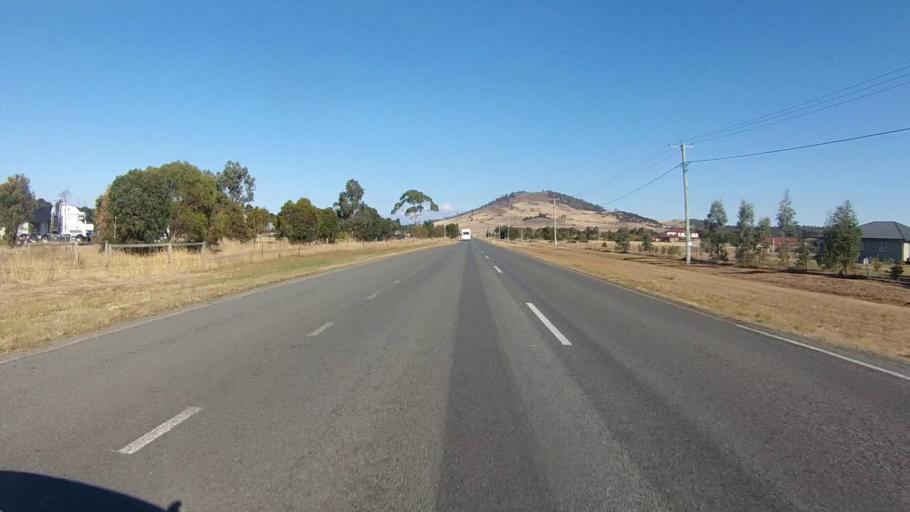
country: AU
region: Tasmania
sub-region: Clarence
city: Seven Mile Beach
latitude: -42.8540
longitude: 147.4876
